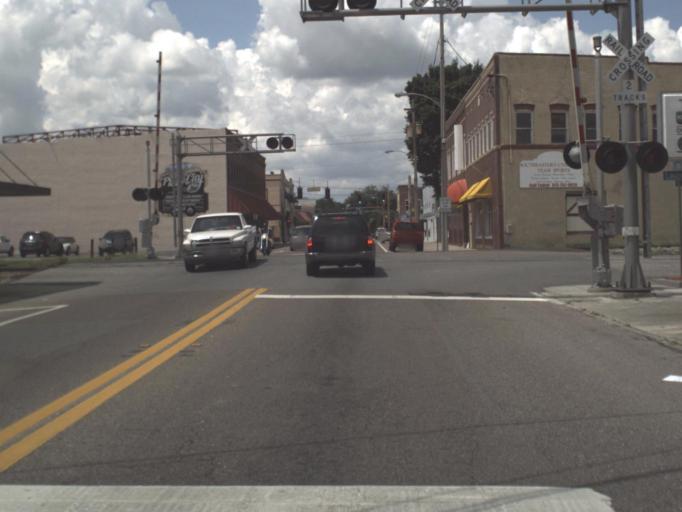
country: US
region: Florida
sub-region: Hillsborough County
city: Plant City
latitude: 28.0133
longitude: -82.1227
